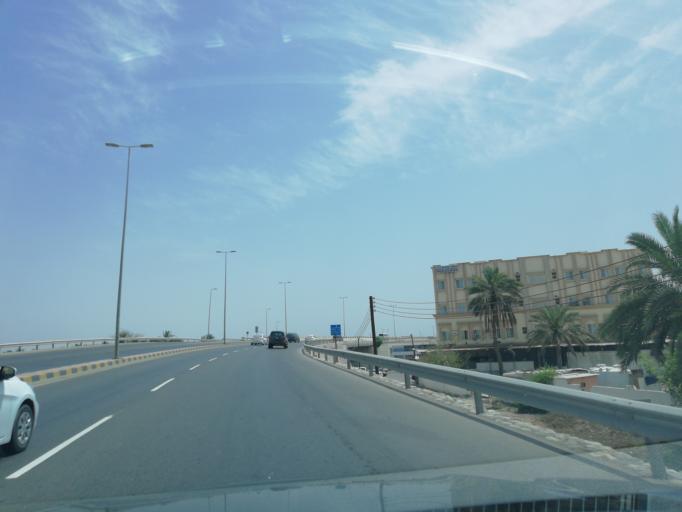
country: OM
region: Muhafazat Masqat
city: As Sib al Jadidah
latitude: 23.6771
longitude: 58.1386
